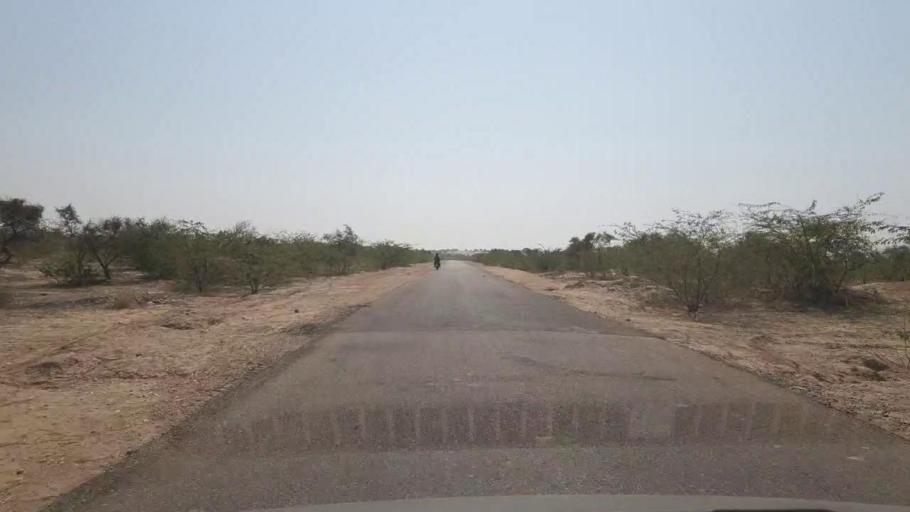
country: PK
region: Sindh
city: Chor
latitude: 25.5913
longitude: 70.1835
